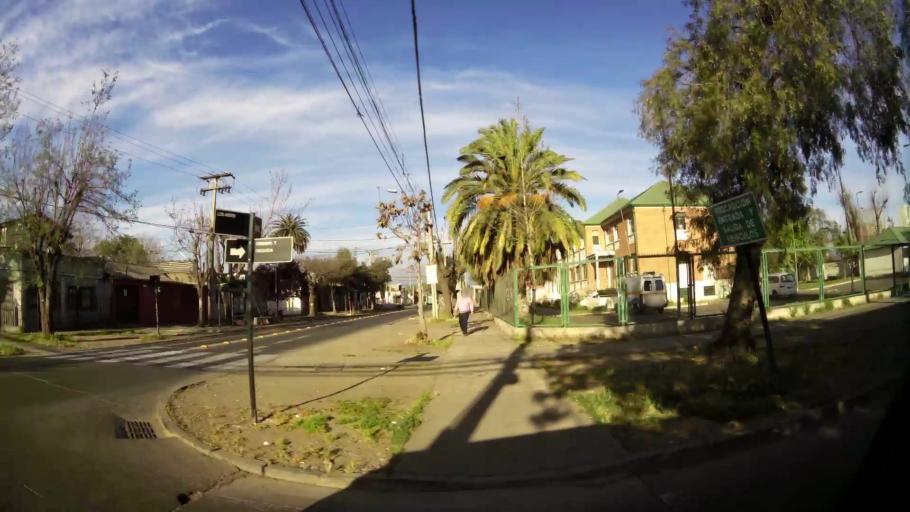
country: CL
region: Santiago Metropolitan
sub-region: Provincia de Santiago
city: Lo Prado
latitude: -33.4339
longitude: -70.6936
